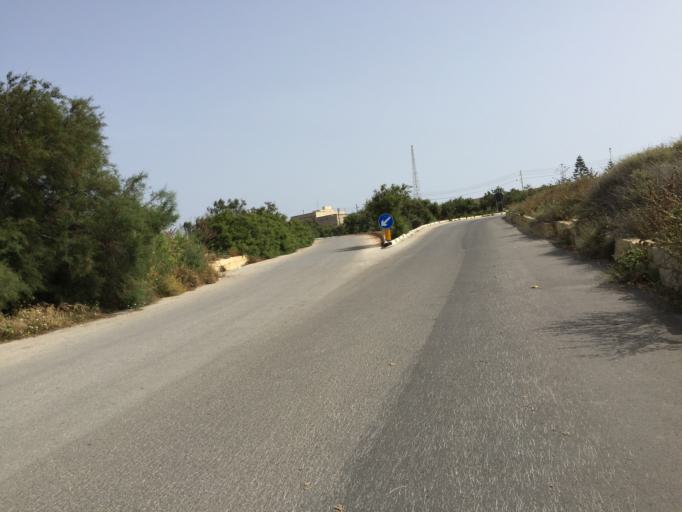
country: MT
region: Il-Kalkara
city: Kalkara
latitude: 35.8956
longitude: 14.5300
